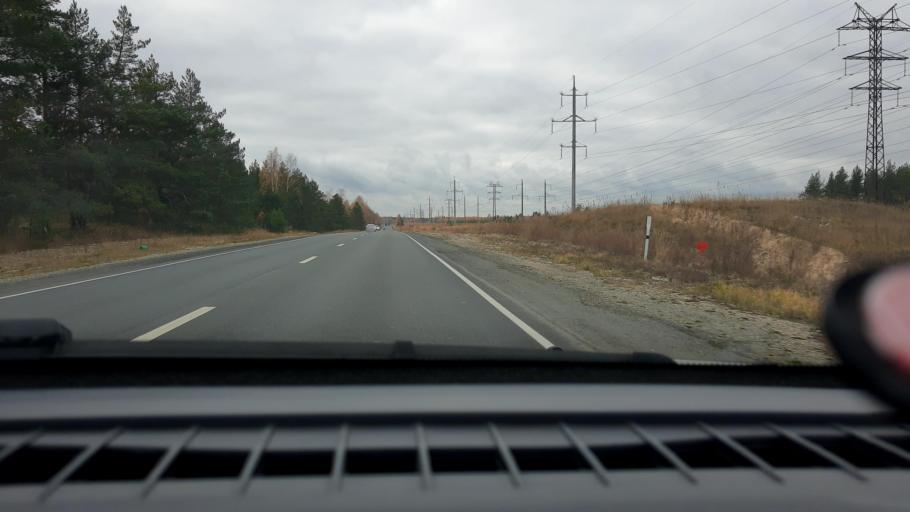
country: RU
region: Nizjnij Novgorod
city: Lukino
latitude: 56.3800
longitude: 43.6299
